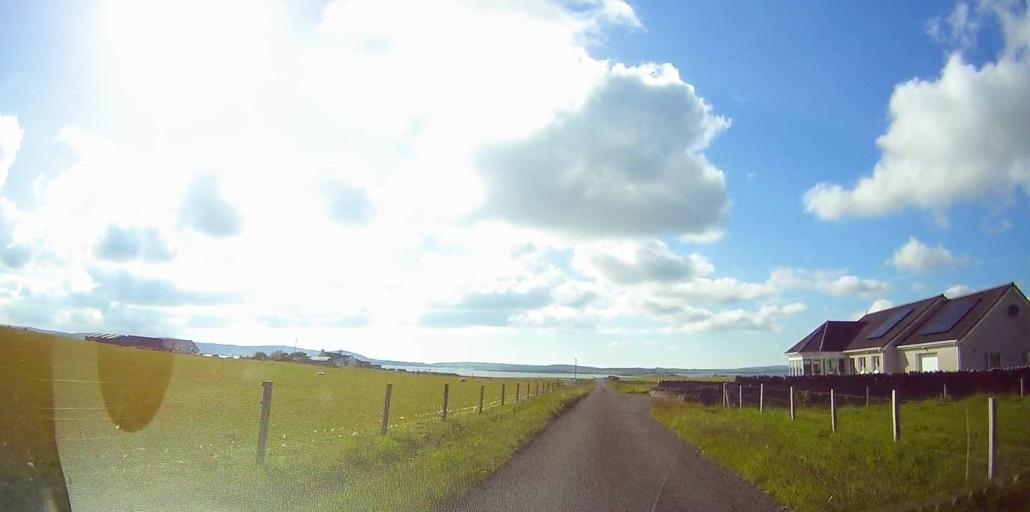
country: GB
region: Scotland
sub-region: Orkney Islands
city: Stromness
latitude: 58.9878
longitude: -3.1958
